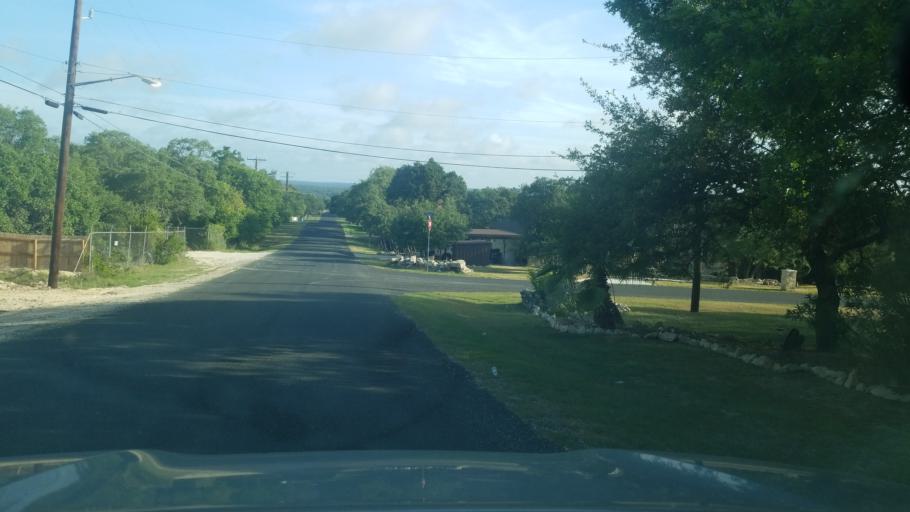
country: US
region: Texas
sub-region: Bexar County
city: Timberwood Park
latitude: 29.7017
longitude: -98.5148
